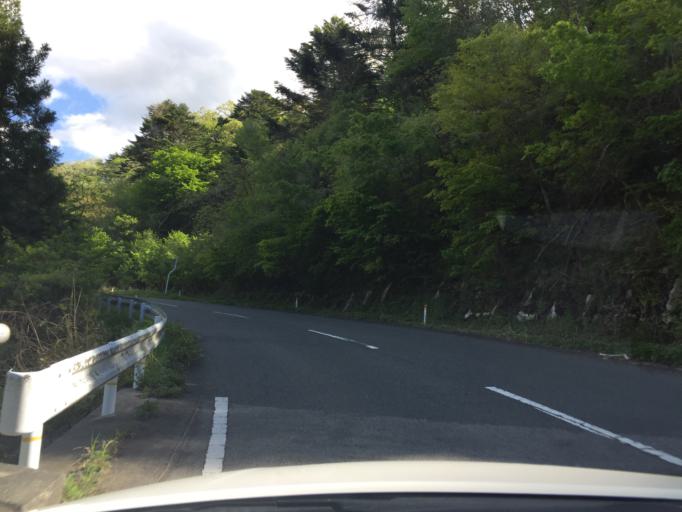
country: JP
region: Miyagi
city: Marumori
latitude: 37.7303
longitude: 140.8024
